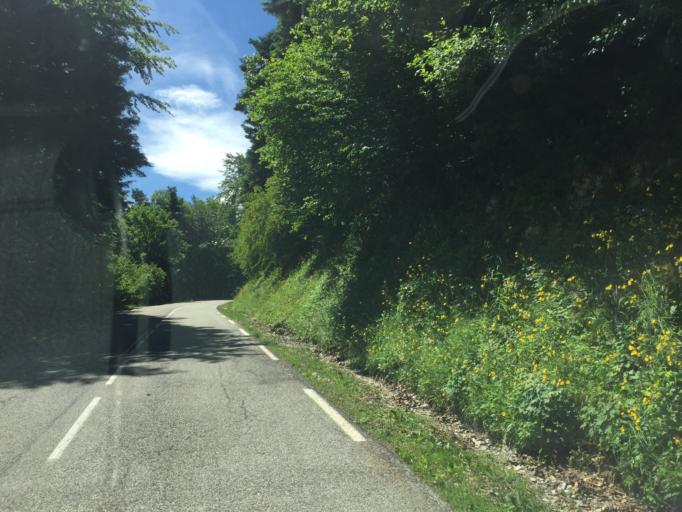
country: FR
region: Rhone-Alpes
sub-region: Departement de la Savoie
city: Saint-Baldoph
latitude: 45.4977
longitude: 5.9173
